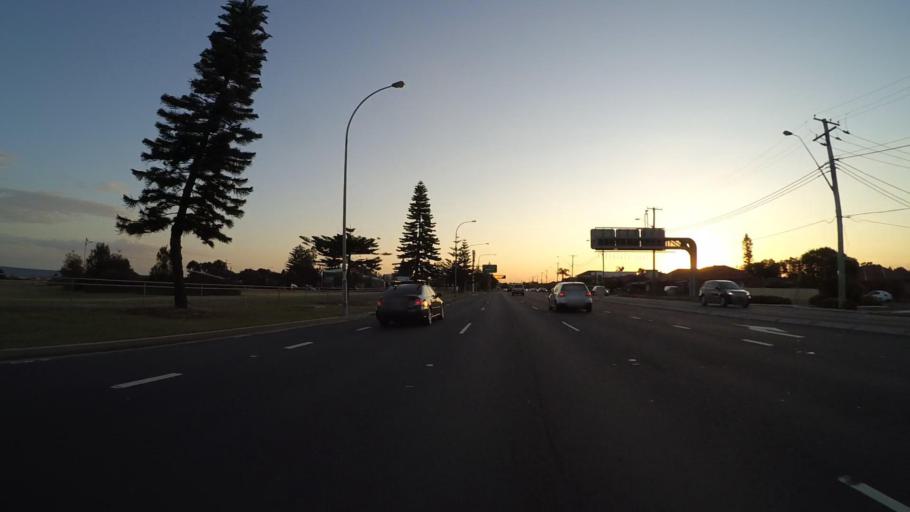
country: AU
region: New South Wales
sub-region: Rockdale
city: Brighton-Le-Sands
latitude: -33.9496
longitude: 151.1644
